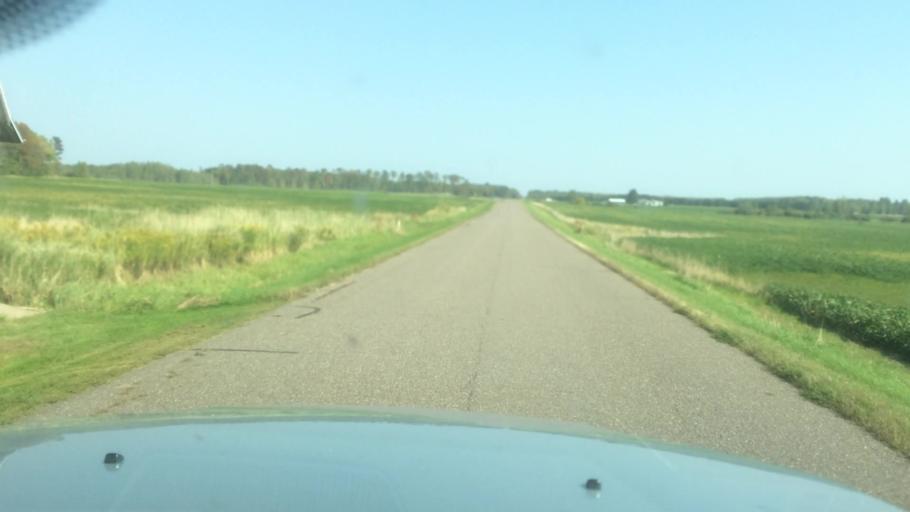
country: US
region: Wisconsin
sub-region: Taylor County
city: Medford
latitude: 45.0914
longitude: -90.3106
